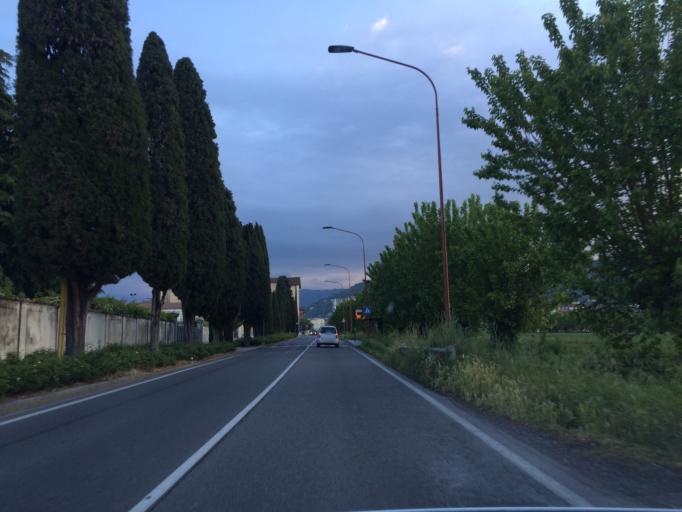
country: IT
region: Lombardy
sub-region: Provincia di Brescia
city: Brescia
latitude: 45.5163
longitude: 10.2279
